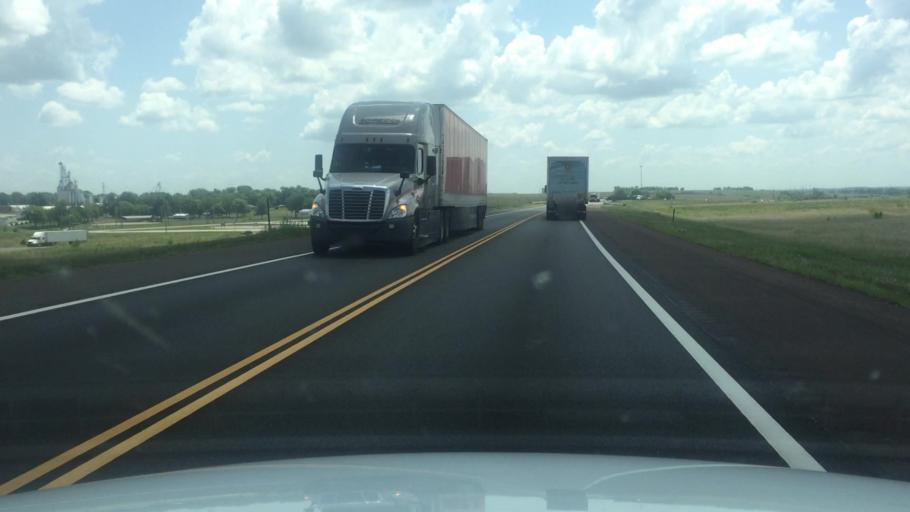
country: US
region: Kansas
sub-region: Nemaha County
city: Sabetha
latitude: 39.8435
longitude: -95.7388
